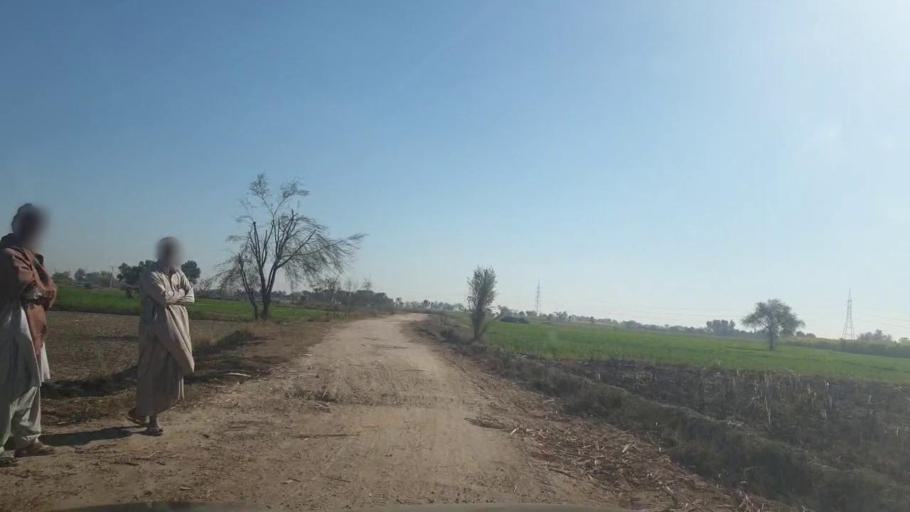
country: PK
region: Sindh
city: Adilpur
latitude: 27.9682
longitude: 69.3382
